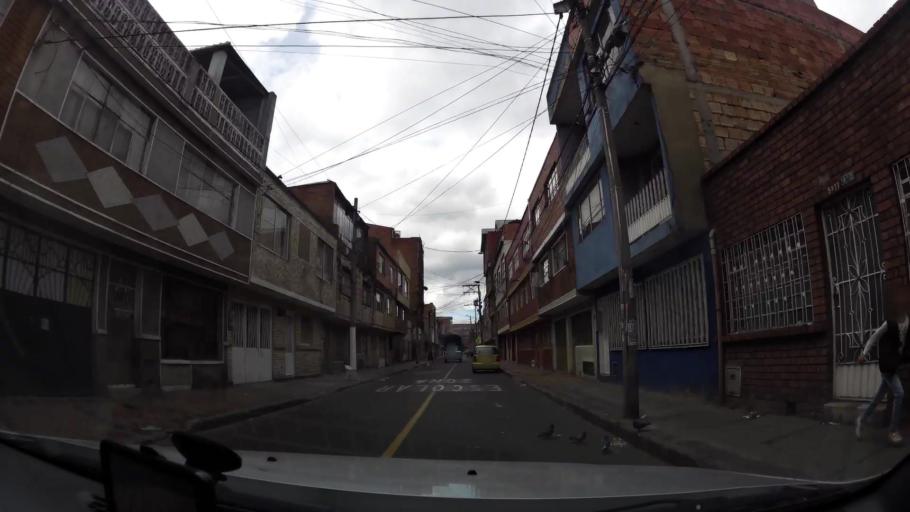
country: CO
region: Bogota D.C.
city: Bogota
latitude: 4.6232
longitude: -74.1181
